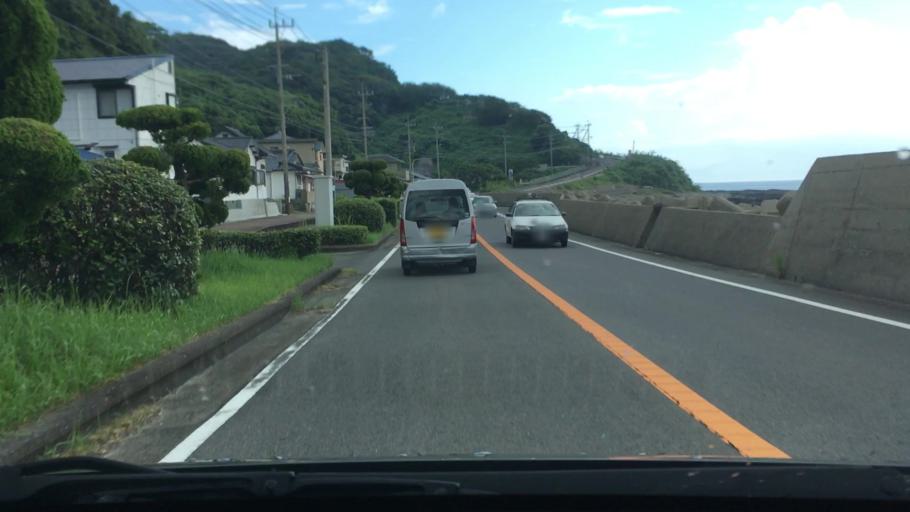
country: JP
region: Nagasaki
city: Togitsu
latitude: 32.8761
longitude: 129.6796
